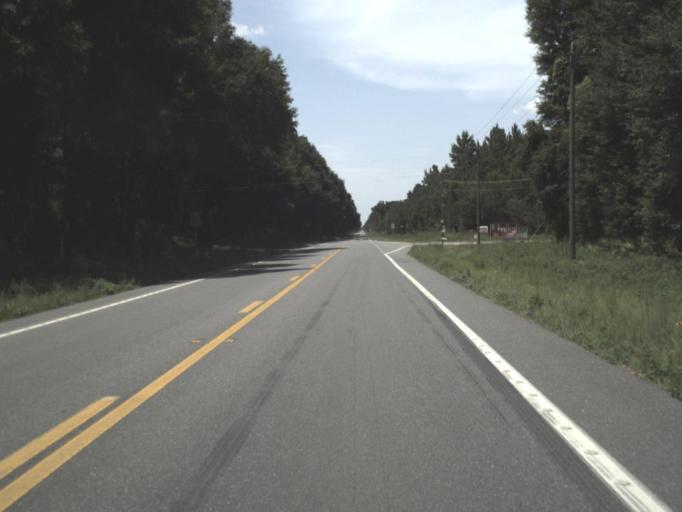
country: US
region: Florida
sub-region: Alachua County
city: High Springs
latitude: 29.8898
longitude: -82.8599
